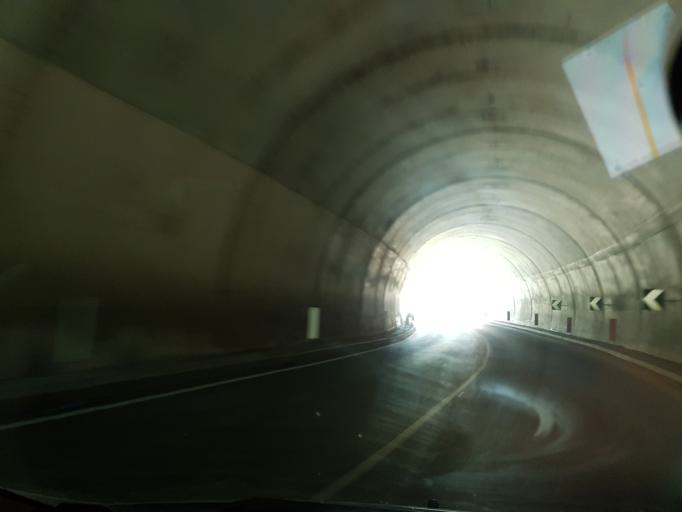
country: IT
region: Tuscany
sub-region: Provincia di Lucca
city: Piazza al Serchio-San Michele
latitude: 44.1814
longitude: 10.3088
